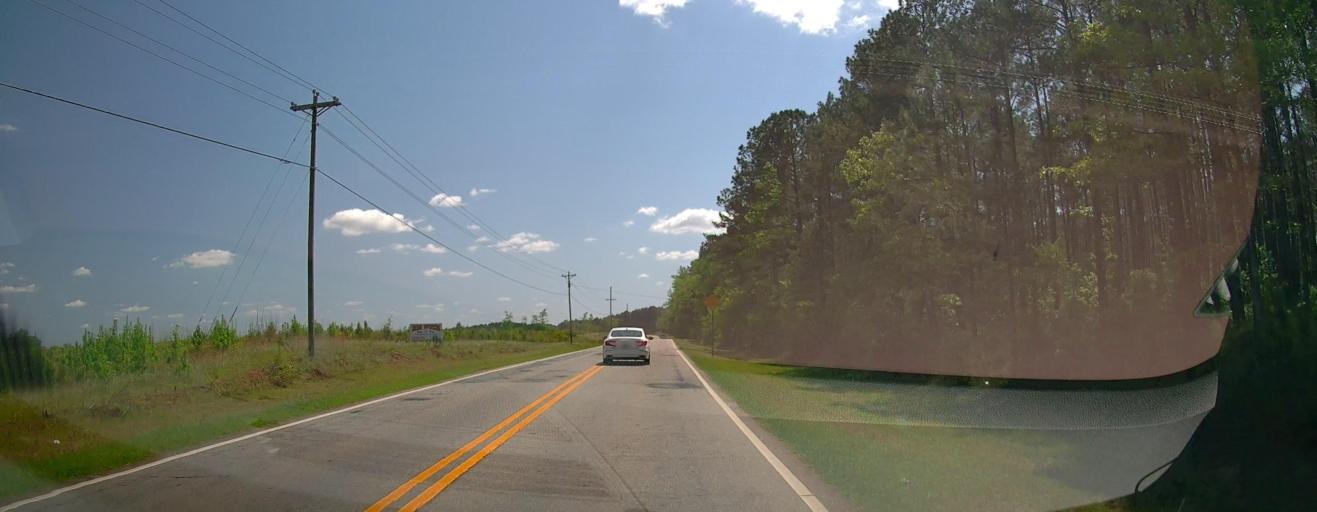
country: US
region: Georgia
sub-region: Putnam County
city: Eatonton
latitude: 33.2565
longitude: -83.3014
